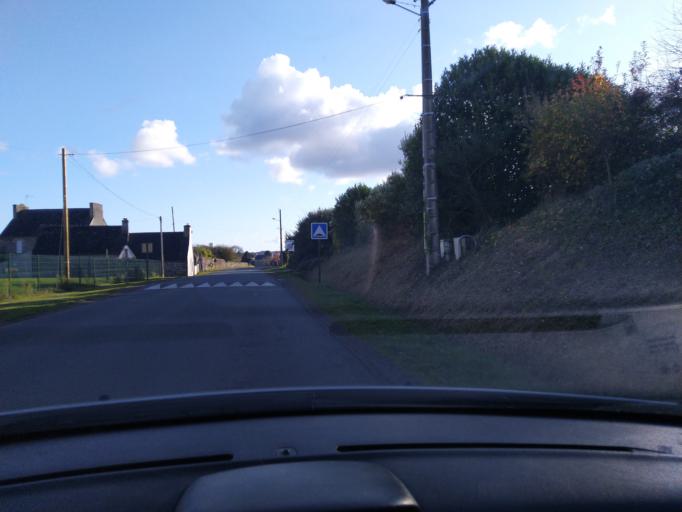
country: FR
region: Brittany
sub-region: Departement des Cotes-d'Armor
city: Plestin-les-Greves
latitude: 48.6020
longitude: -3.6101
